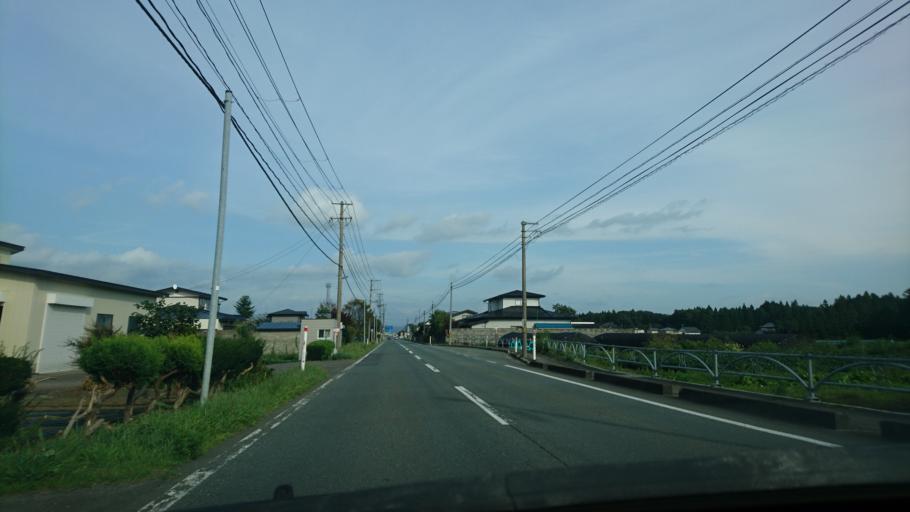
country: JP
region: Iwate
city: Kitakami
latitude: 39.3040
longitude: 141.0174
